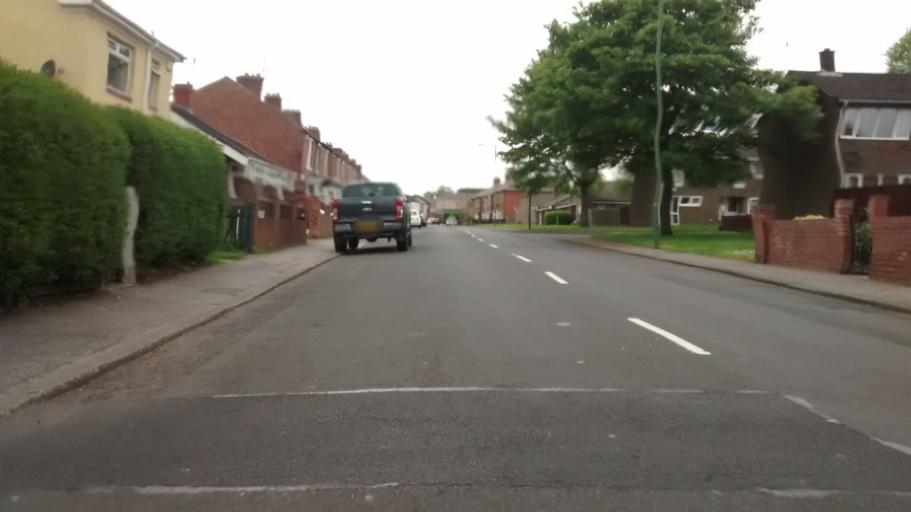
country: GB
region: England
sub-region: County Durham
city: Durham
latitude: 54.7780
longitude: -1.5498
